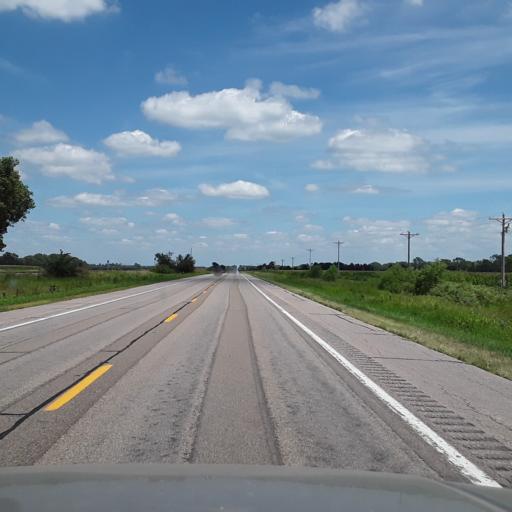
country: US
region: Nebraska
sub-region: Nance County
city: Genoa
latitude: 41.3312
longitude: -97.6273
